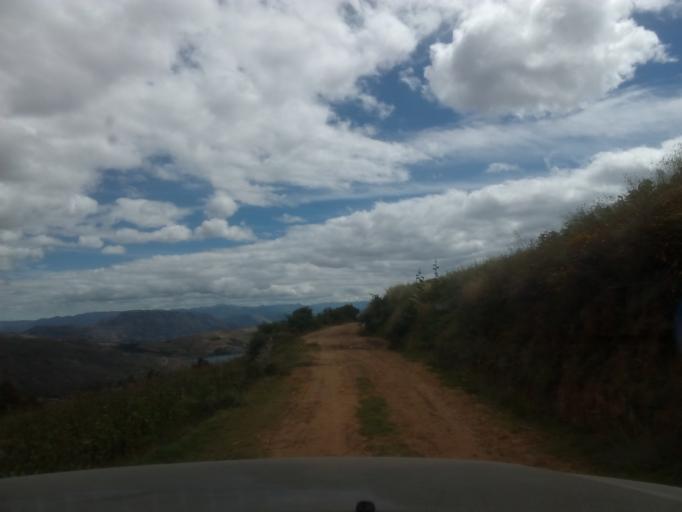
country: PE
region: La Libertad
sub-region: Sanchez Carrion
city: Curgos
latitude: -7.8055
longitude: -77.9695
